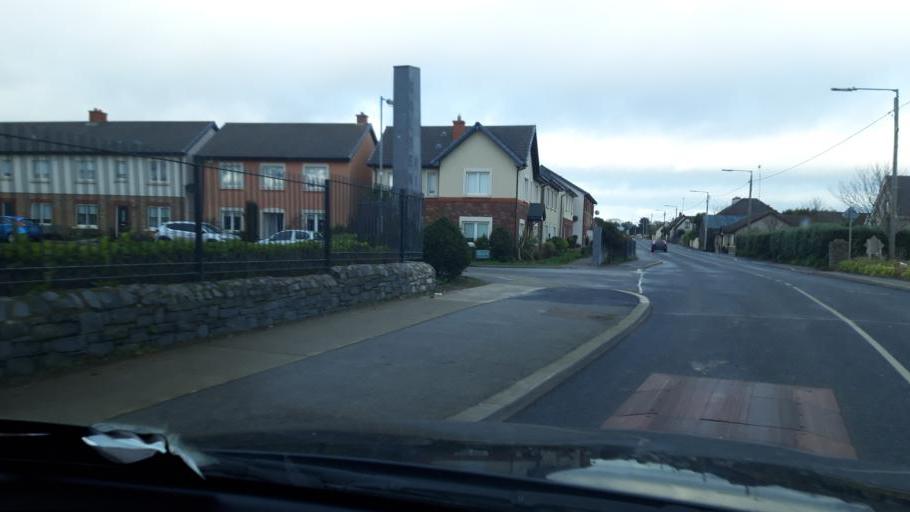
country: IE
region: Leinster
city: An Ros
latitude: 53.5248
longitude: -6.0913
